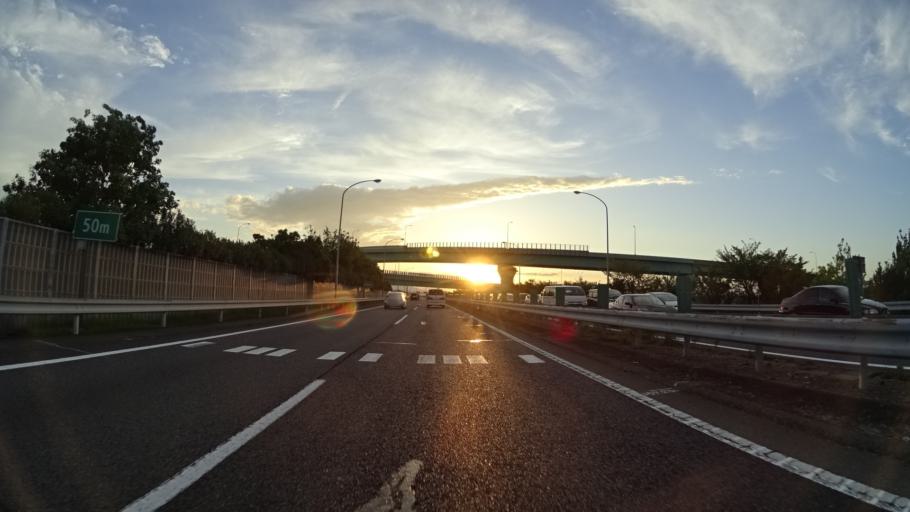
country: JP
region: Aichi
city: Ichinomiya
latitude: 35.2824
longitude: 136.7830
